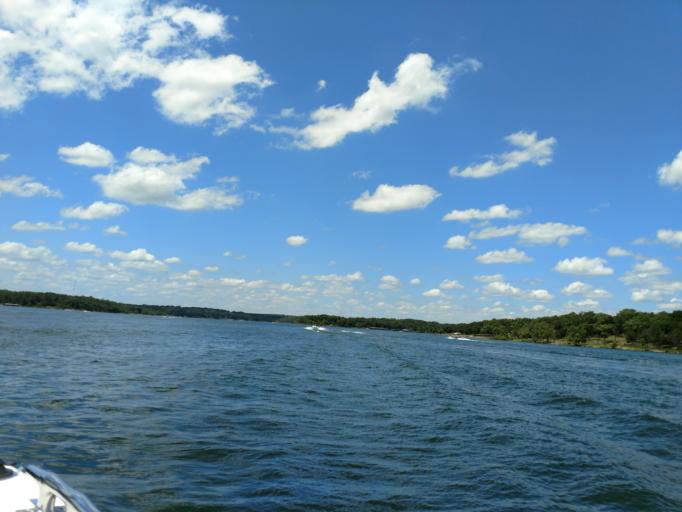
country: US
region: Missouri
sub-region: Barry County
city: Shell Knob
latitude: 36.5896
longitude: -93.5552
